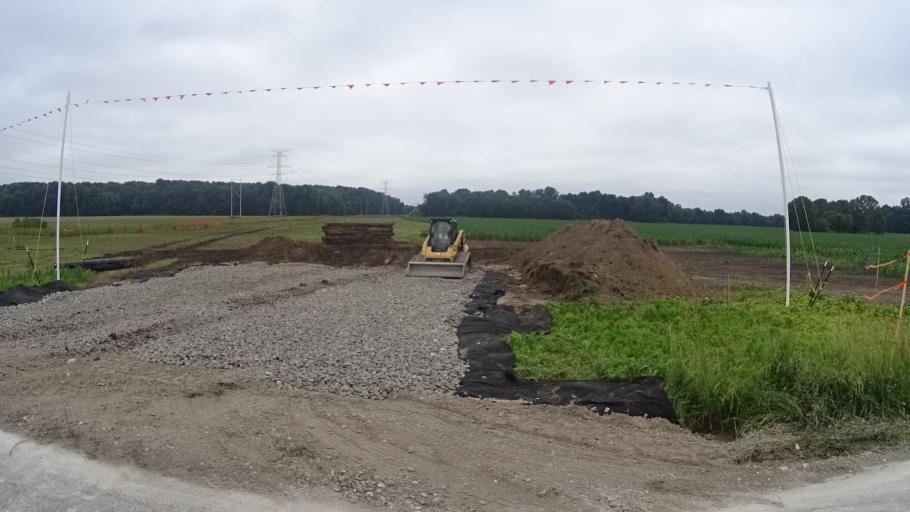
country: US
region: Ohio
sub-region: Erie County
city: Huron
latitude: 41.3372
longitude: -82.5438
